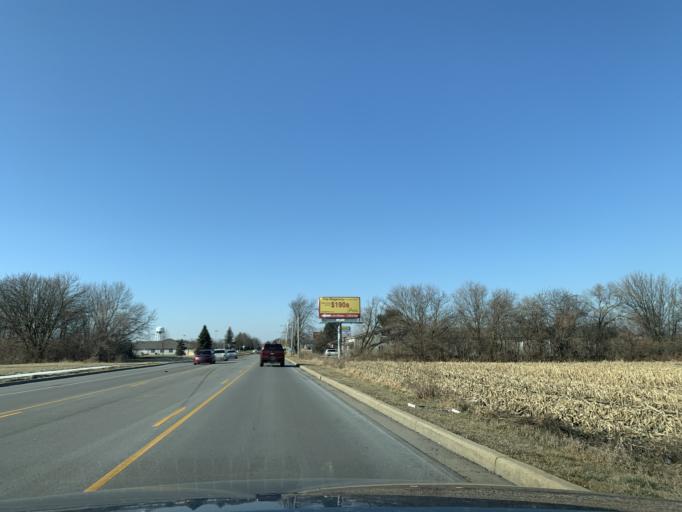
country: US
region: Indiana
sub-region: Lake County
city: Crown Point
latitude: 41.4202
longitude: -87.3378
